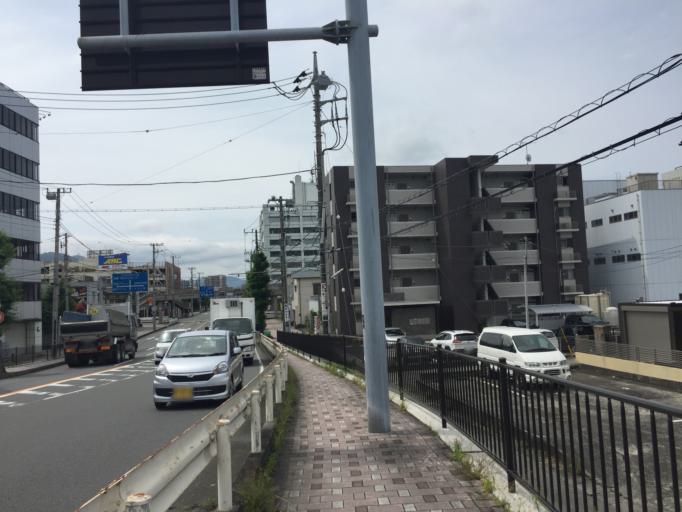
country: JP
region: Shizuoka
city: Numazu
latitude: 35.0974
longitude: 138.8631
